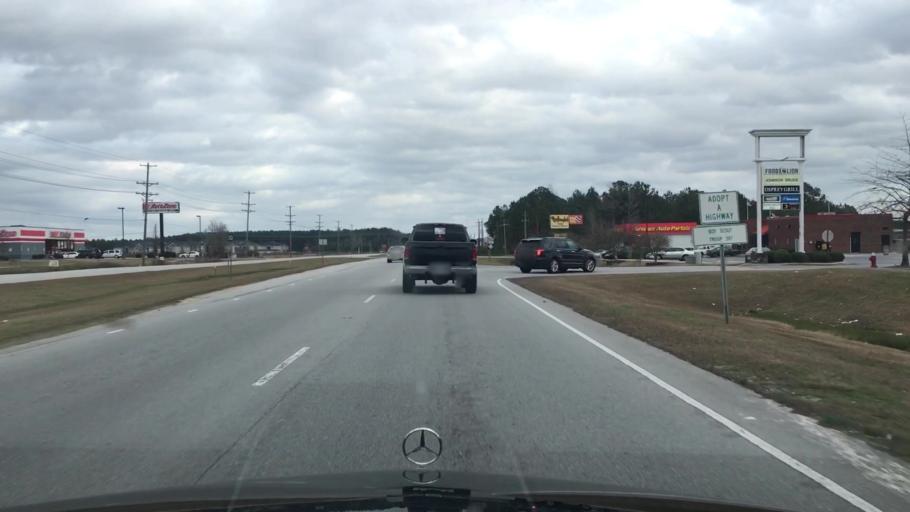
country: US
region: North Carolina
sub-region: Onslow County
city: Half Moon
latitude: 34.7995
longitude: -77.4385
